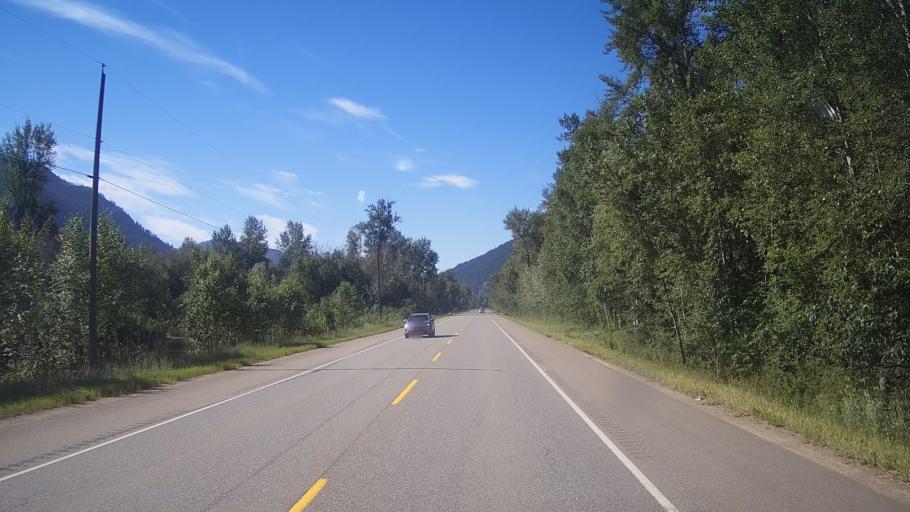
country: CA
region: British Columbia
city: Chase
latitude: 51.5063
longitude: -120.1752
